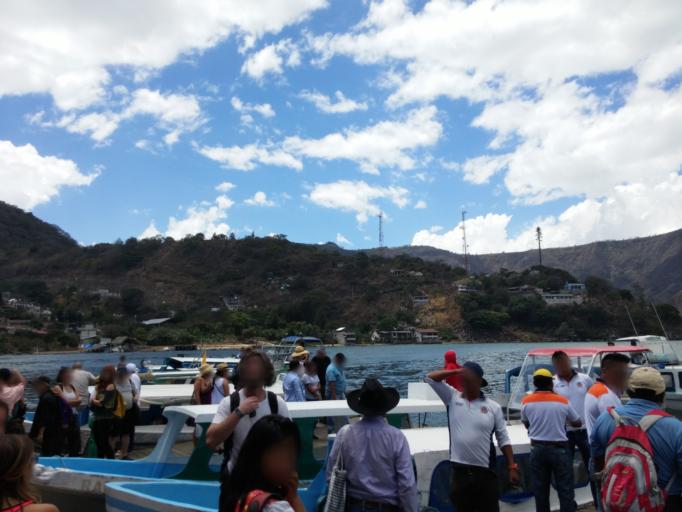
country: GT
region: Solola
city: San Pedro La Laguna
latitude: 14.6950
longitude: -91.2739
